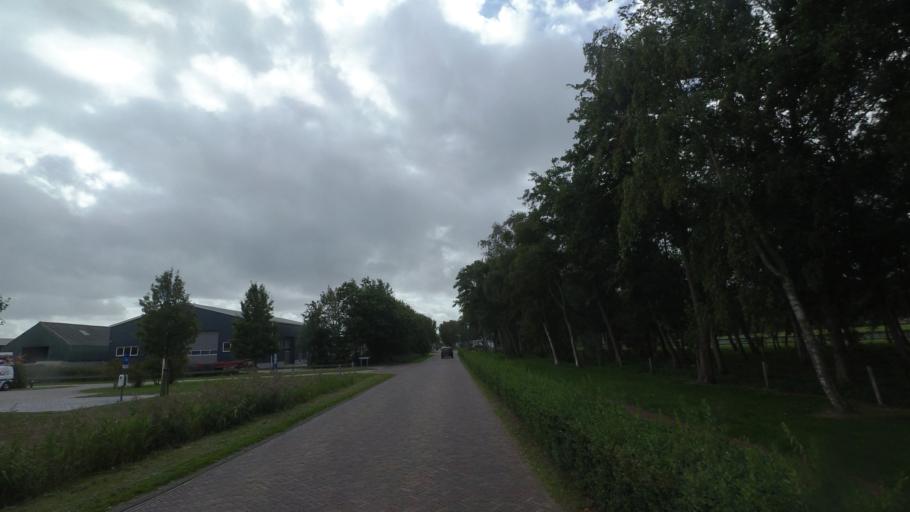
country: NL
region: Friesland
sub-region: Gemeente Ameland
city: Hollum
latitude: 53.4452
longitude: 5.6407
